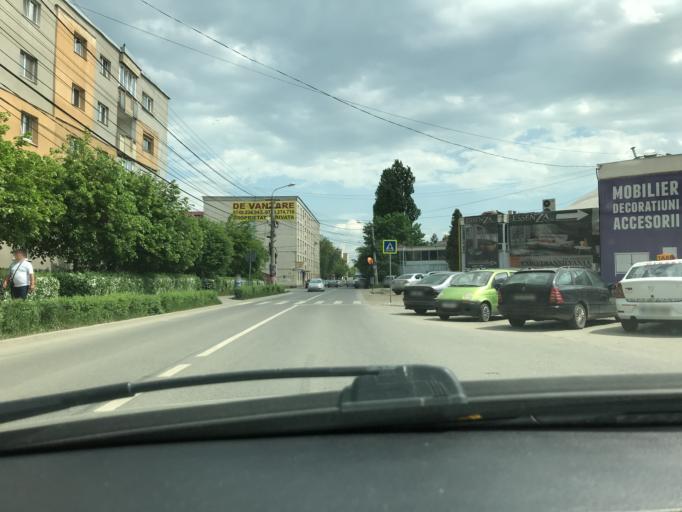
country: RO
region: Cluj
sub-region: Municipiul Cluj-Napoca
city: Cluj-Napoca
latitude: 46.7821
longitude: 23.6291
